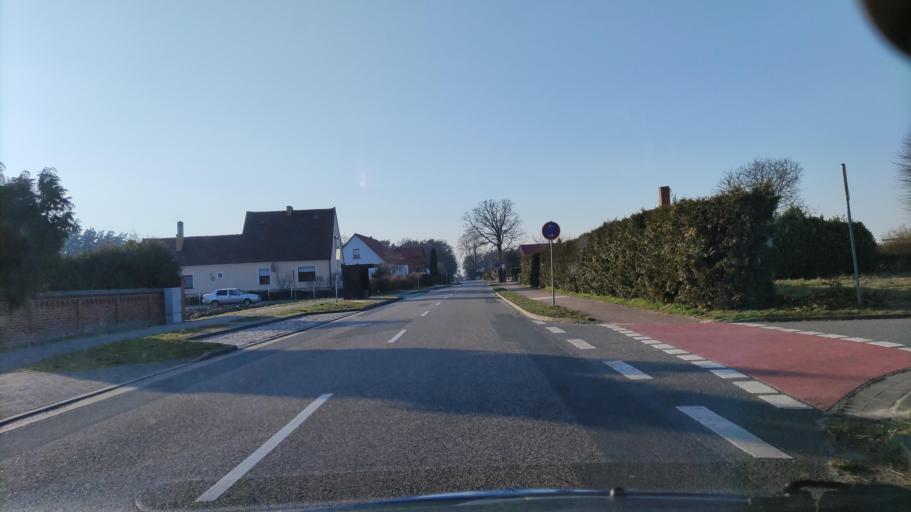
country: DE
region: Saxony-Anhalt
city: Seehausen
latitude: 52.9243
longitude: 11.6879
